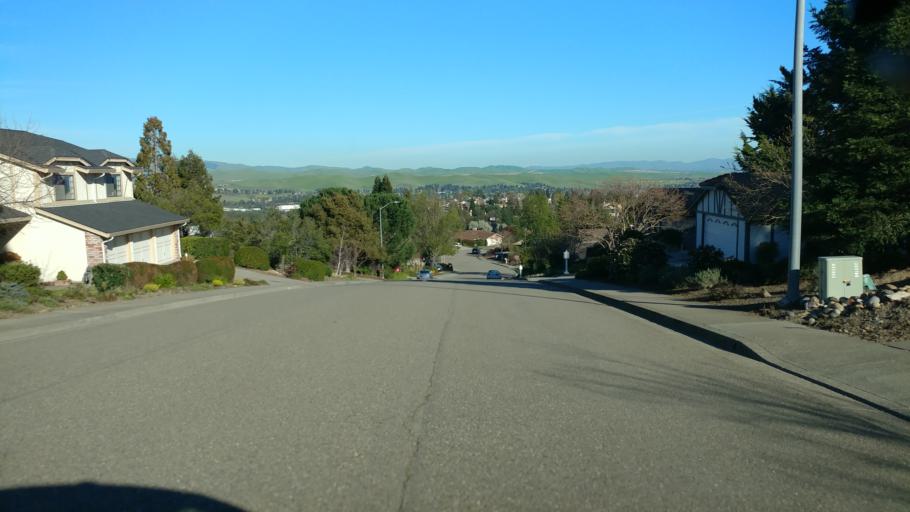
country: US
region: California
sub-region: Contra Costa County
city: San Ramon
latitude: 37.7567
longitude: -121.9822
